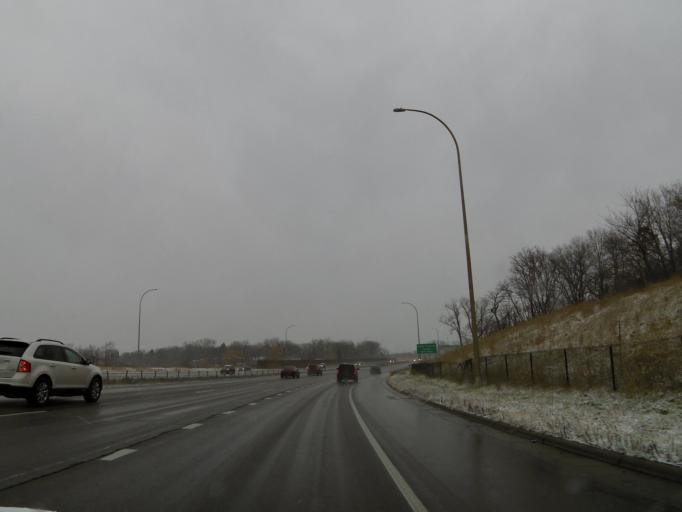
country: US
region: Minnesota
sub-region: Hennepin County
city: Edina
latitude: 44.8507
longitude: -93.3980
